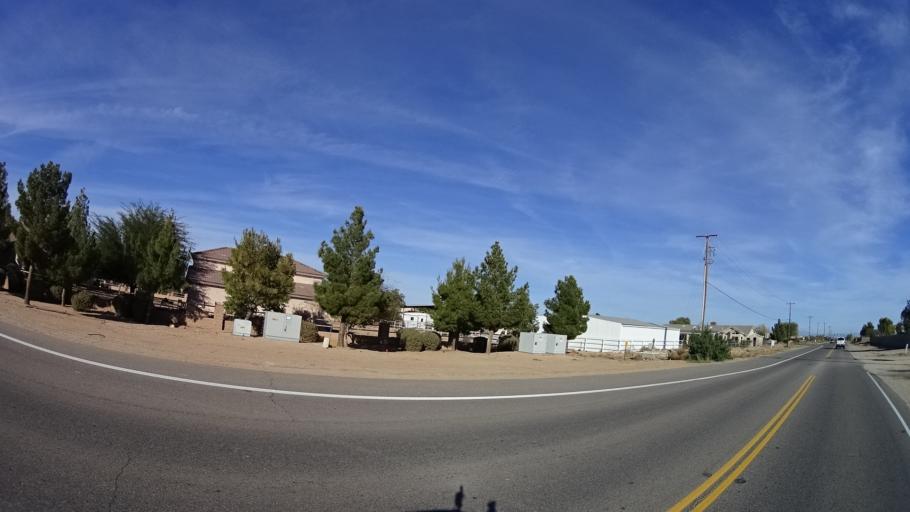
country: US
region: Arizona
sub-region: Maricopa County
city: Queen Creek
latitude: 33.2195
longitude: -111.6739
